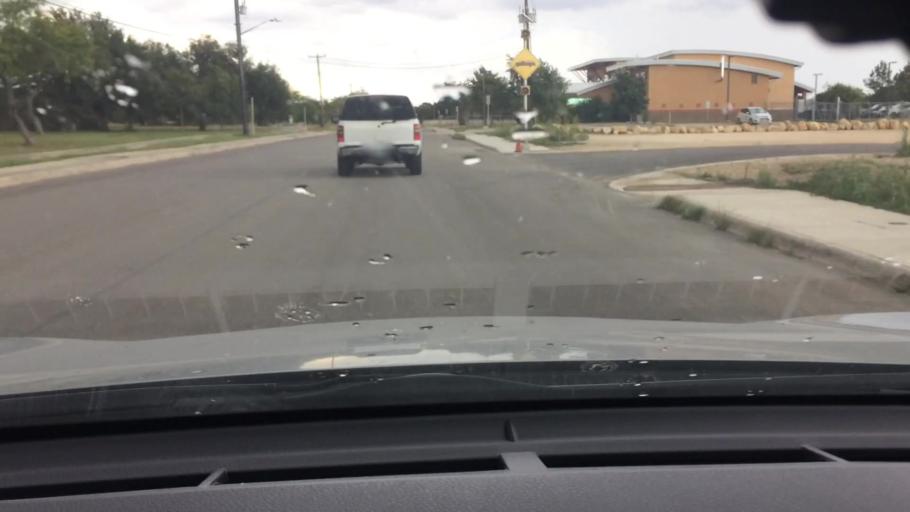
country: US
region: Texas
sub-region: Bexar County
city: Shavano Park
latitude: 29.5730
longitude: -98.5886
